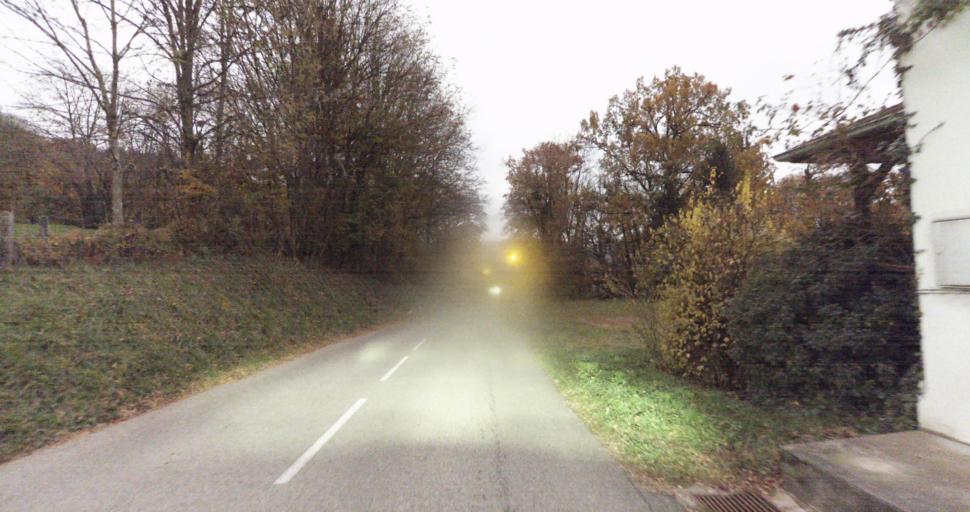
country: FR
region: Rhone-Alpes
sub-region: Departement de la Haute-Savoie
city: Alby-sur-Cheran
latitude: 45.8365
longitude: 6.0093
